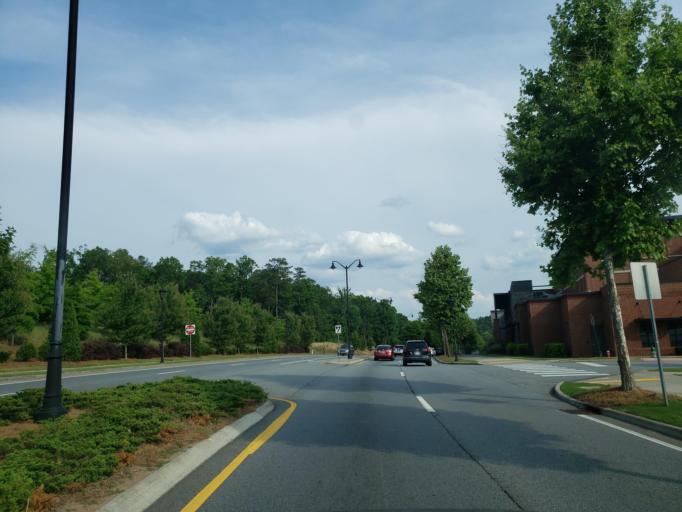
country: US
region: Georgia
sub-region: Cherokee County
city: Woodstock
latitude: 34.1188
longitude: -84.5168
